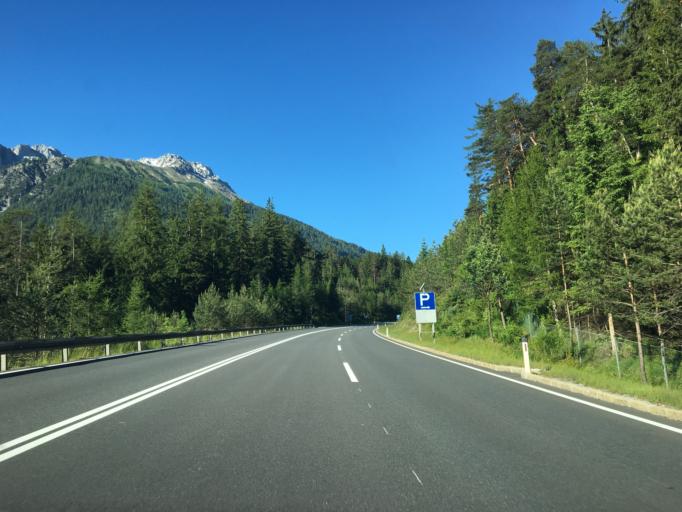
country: AT
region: Tyrol
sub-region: Politischer Bezirk Reutte
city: Biberwier
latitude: 47.3724
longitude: 10.8808
